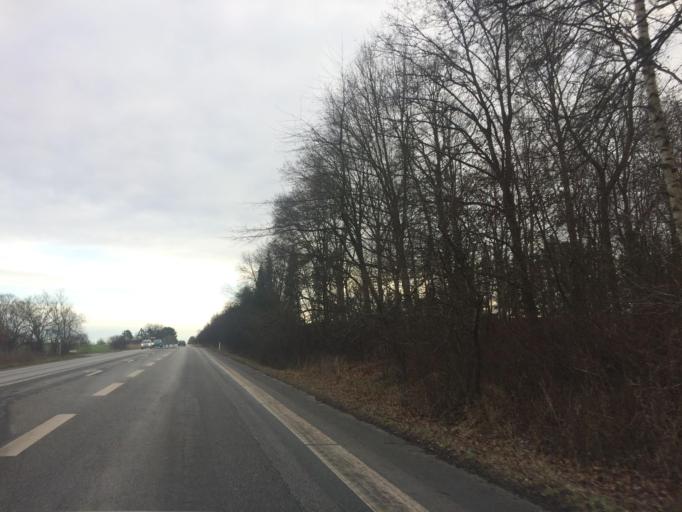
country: DK
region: Capital Region
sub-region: Fredensborg Kommune
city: Fredensborg
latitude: 55.9637
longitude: 12.4077
